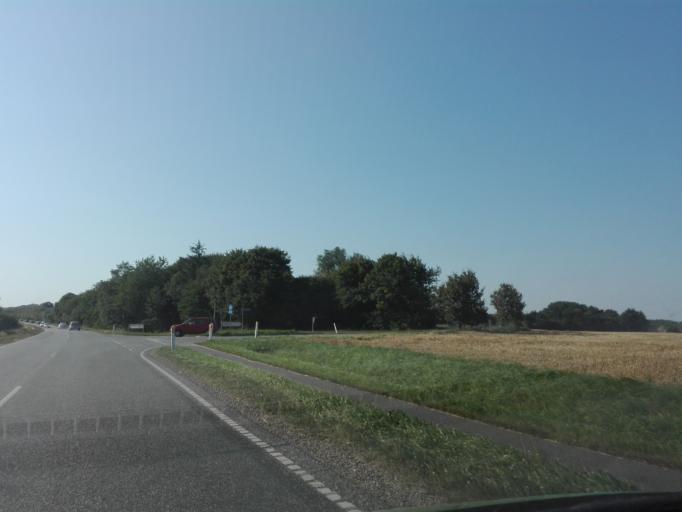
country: DK
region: Central Jutland
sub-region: Odder Kommune
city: Odder
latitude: 55.9637
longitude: 10.1691
